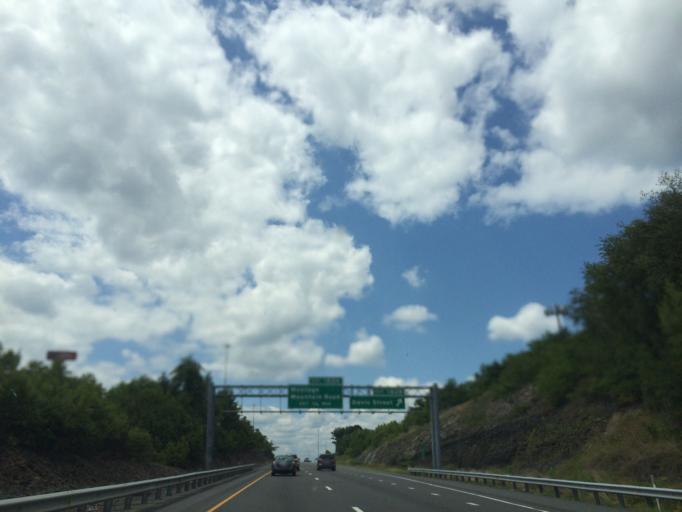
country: US
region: Pennsylvania
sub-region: Lackawanna County
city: Taylor
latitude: 41.3732
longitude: -75.6765
